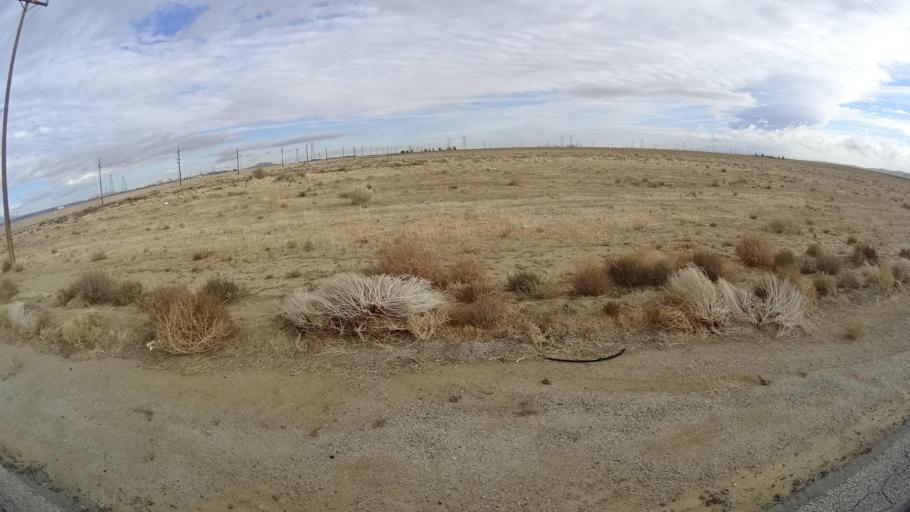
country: US
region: California
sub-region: Los Angeles County
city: Green Valley
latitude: 34.8251
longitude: -118.4316
